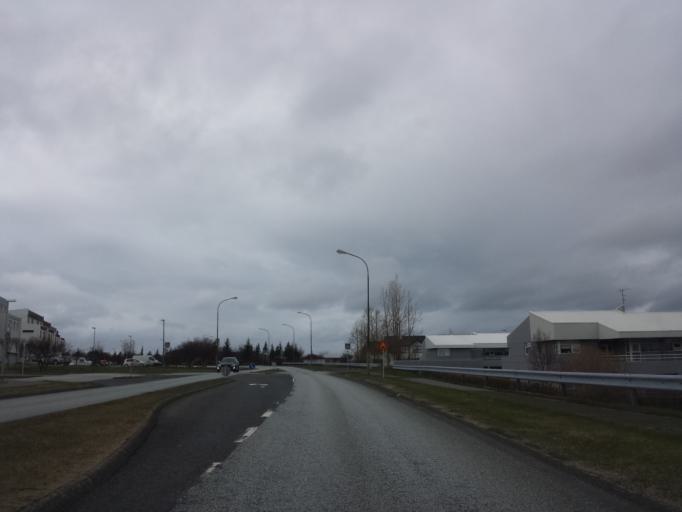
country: IS
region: Capital Region
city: Gardabaer
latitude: 64.0917
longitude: -21.9133
